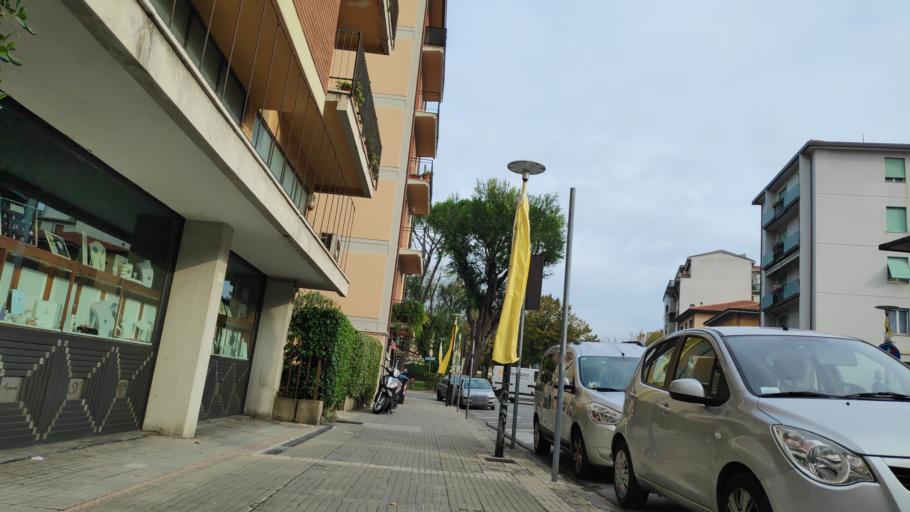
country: IT
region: Tuscany
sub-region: Province of Pisa
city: Pisa
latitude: 43.7044
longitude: 10.4011
